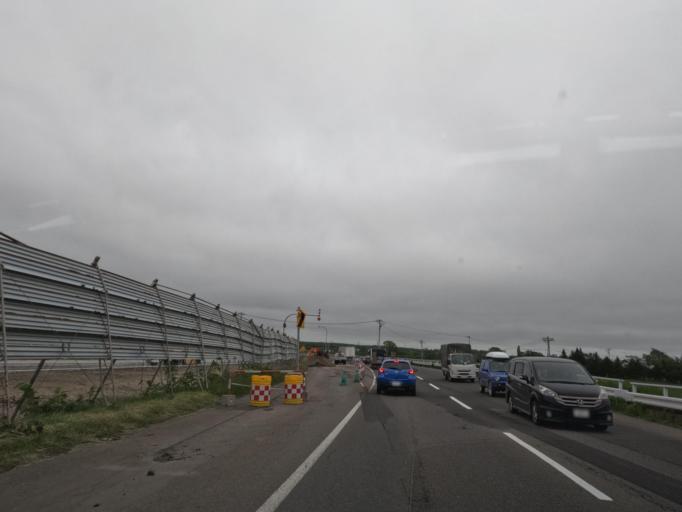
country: JP
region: Hokkaido
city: Ebetsu
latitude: 43.1400
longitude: 141.5154
